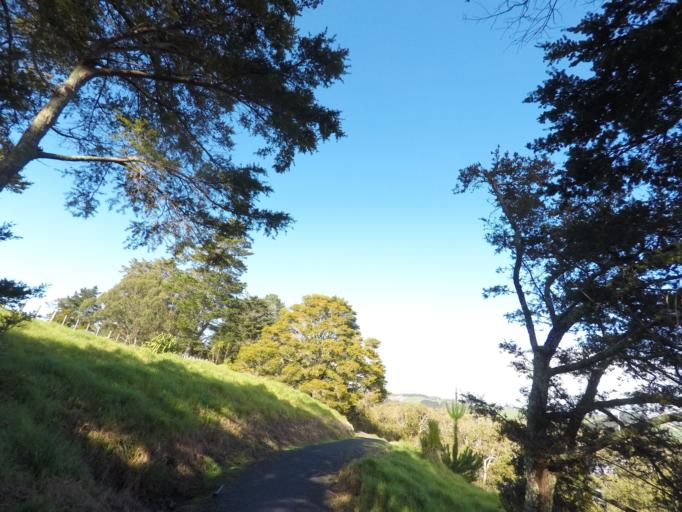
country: NZ
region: Auckland
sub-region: Auckland
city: Warkworth
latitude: -36.4294
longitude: 174.7185
